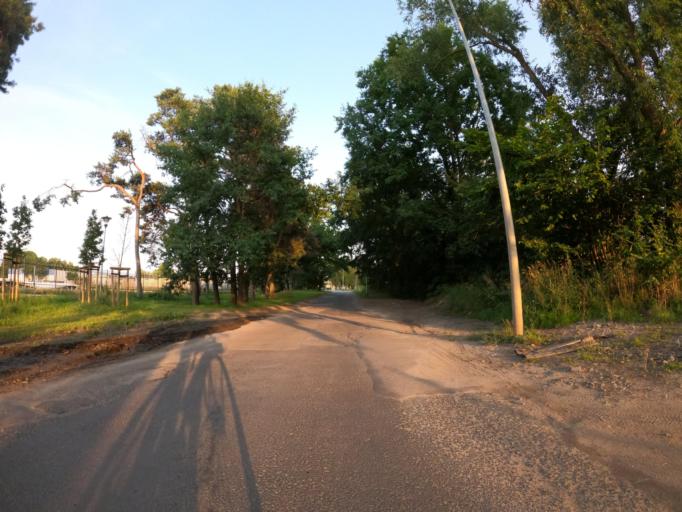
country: PL
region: West Pomeranian Voivodeship
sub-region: Szczecin
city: Szczecin
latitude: 53.4545
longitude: 14.5023
